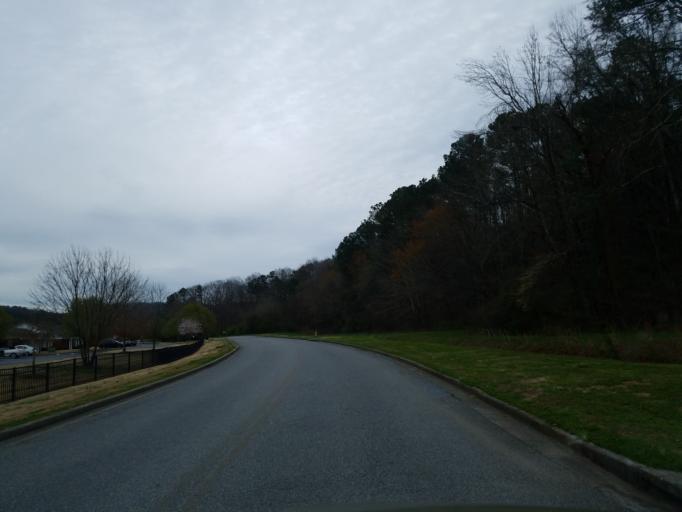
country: US
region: Georgia
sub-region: Bartow County
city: Cartersville
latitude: 34.2147
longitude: -84.7838
